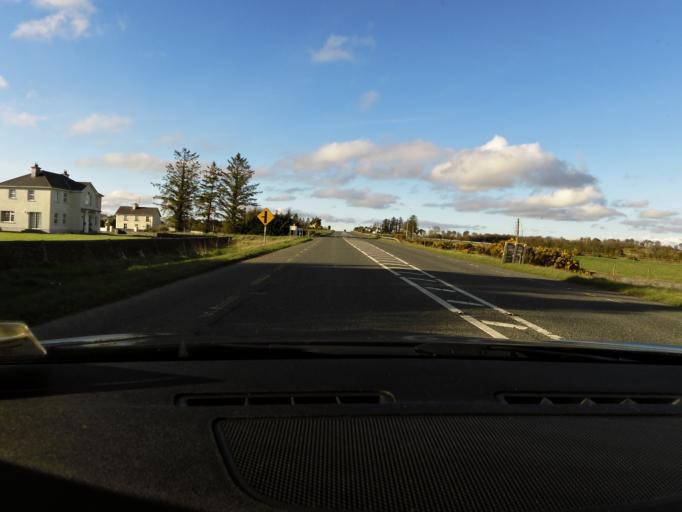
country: IE
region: Connaught
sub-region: Roscommon
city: Roscommon
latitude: 53.6652
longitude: -8.1981
